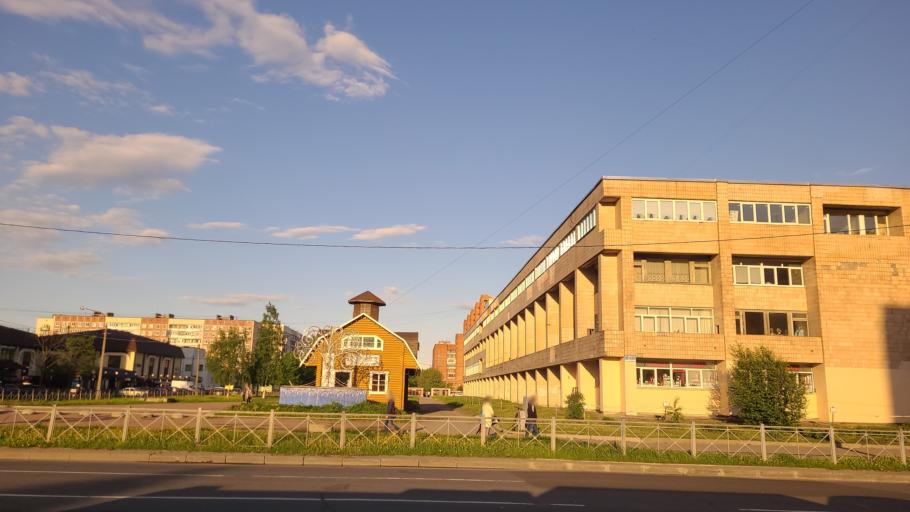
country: RU
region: St.-Petersburg
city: Kolpino
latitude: 59.7351
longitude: 30.5790
